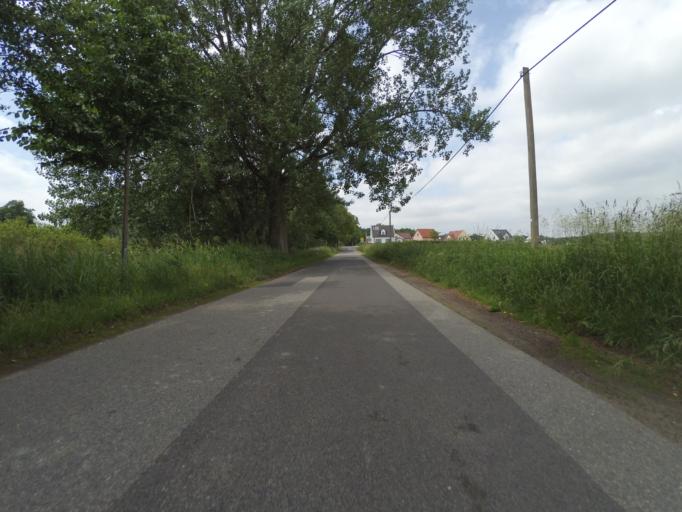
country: DE
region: Mecklenburg-Vorpommern
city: Klink
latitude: 53.4779
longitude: 12.5224
